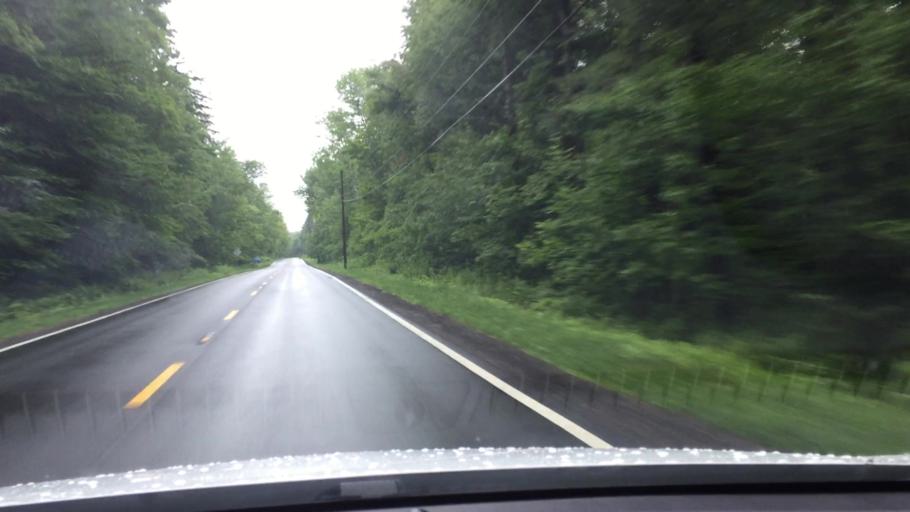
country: US
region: Massachusetts
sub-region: Berkshire County
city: Becket
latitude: 42.3522
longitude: -73.1272
